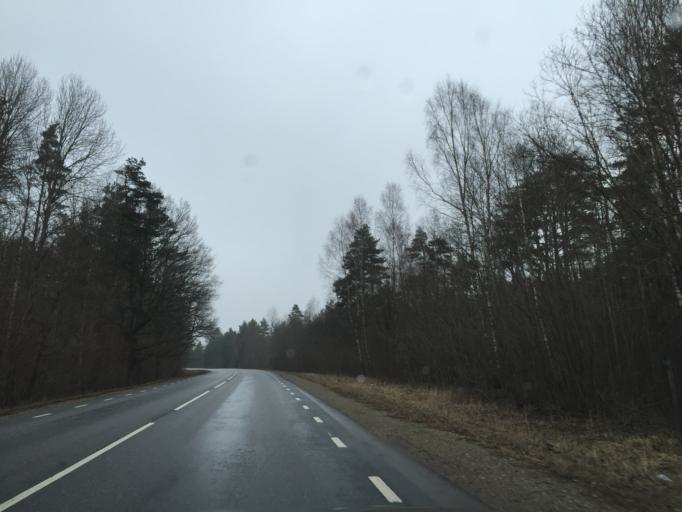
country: EE
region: Laeaene
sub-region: Lihula vald
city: Lihula
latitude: 58.6094
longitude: 23.6957
